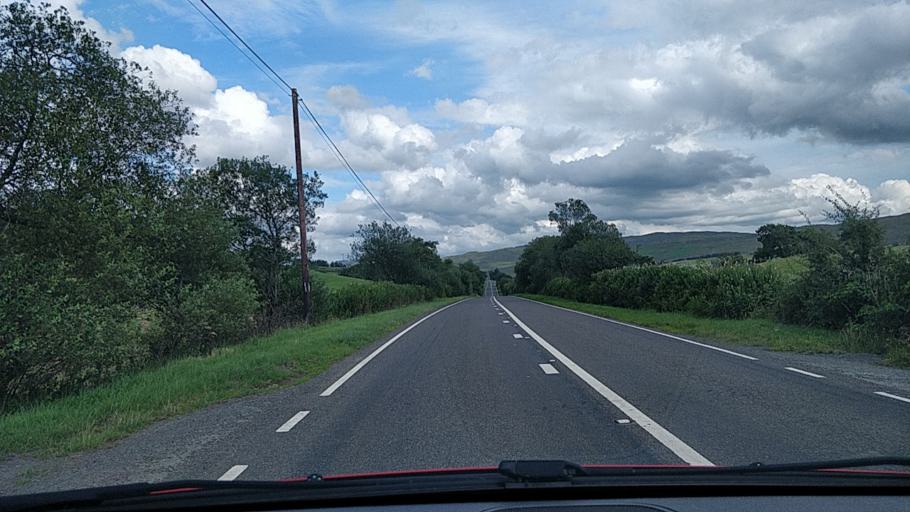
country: GB
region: Wales
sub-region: Gwynedd
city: Trawsfynydd
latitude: 52.9065
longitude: -3.9012
